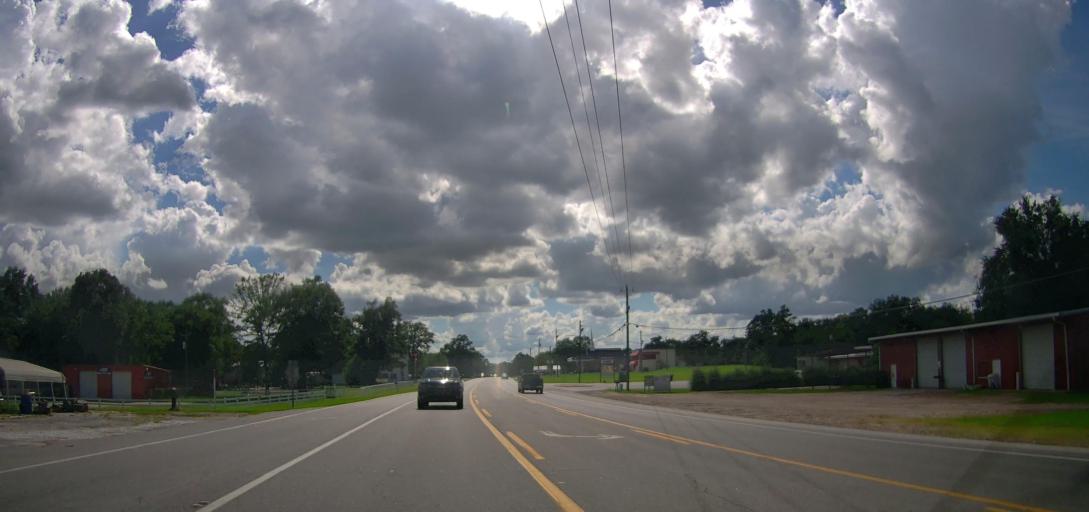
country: US
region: Alabama
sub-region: Russell County
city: Ladonia
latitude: 32.4568
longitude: -85.1868
